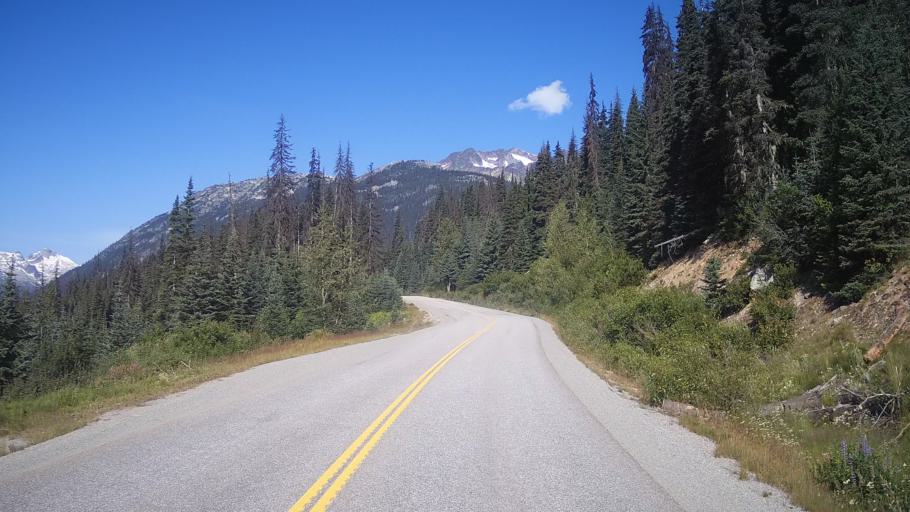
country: CA
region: British Columbia
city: Pemberton
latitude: 50.3864
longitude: -122.4506
